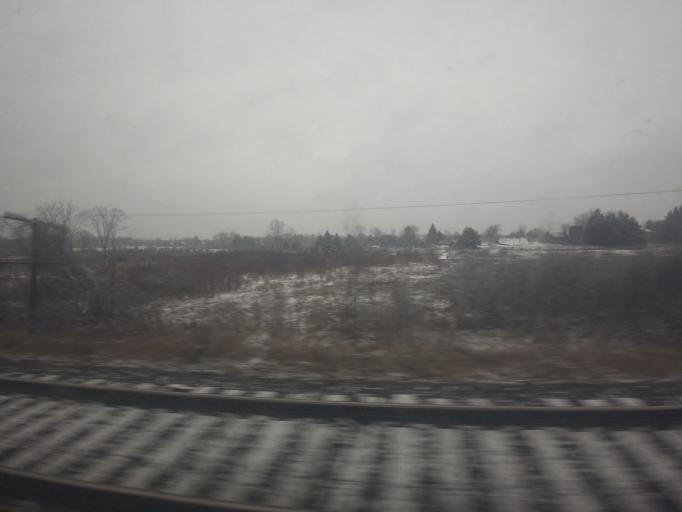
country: US
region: New York
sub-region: Jefferson County
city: Alexandria Bay
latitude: 44.4686
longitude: -75.8984
